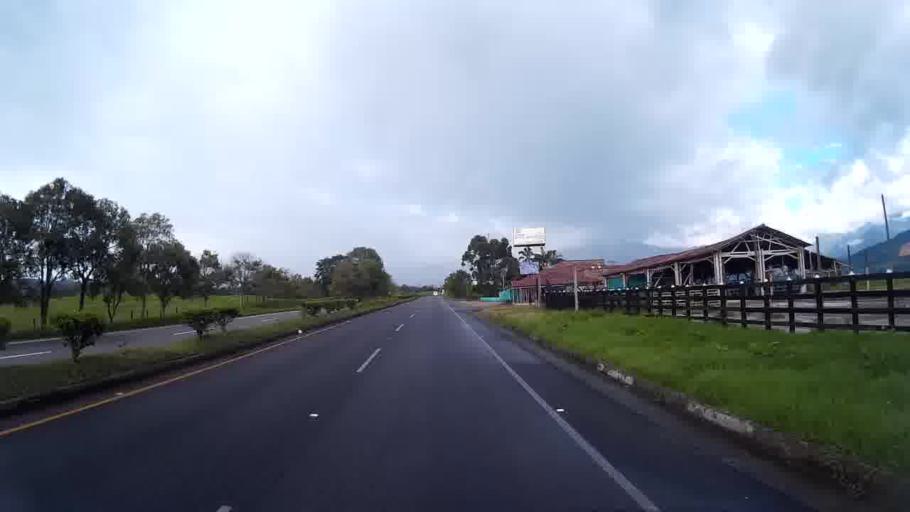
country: CO
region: Quindio
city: Salento
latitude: 4.6451
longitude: -75.6070
